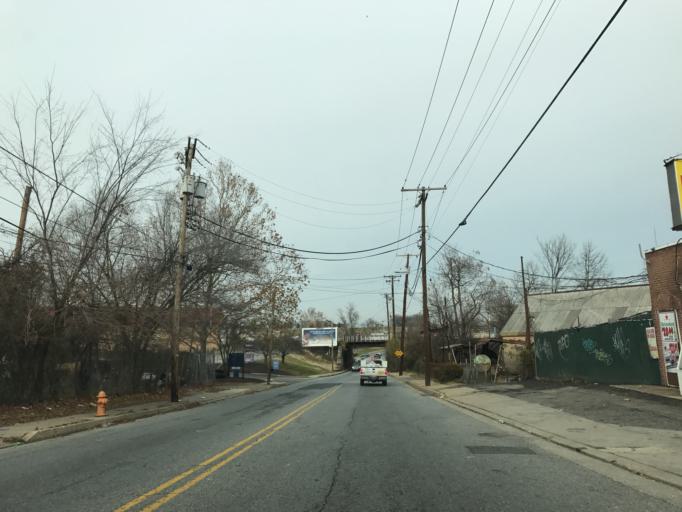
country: US
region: Maryland
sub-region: Baltimore County
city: Baltimore Highlands
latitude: 39.2538
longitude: -76.6388
